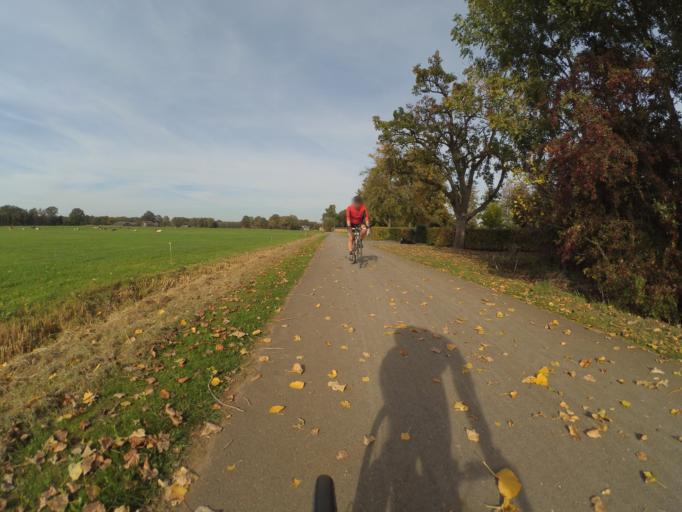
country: NL
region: Gelderland
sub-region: Gemeente Lochem
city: Harfsen
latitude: 52.2366
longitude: 6.3347
